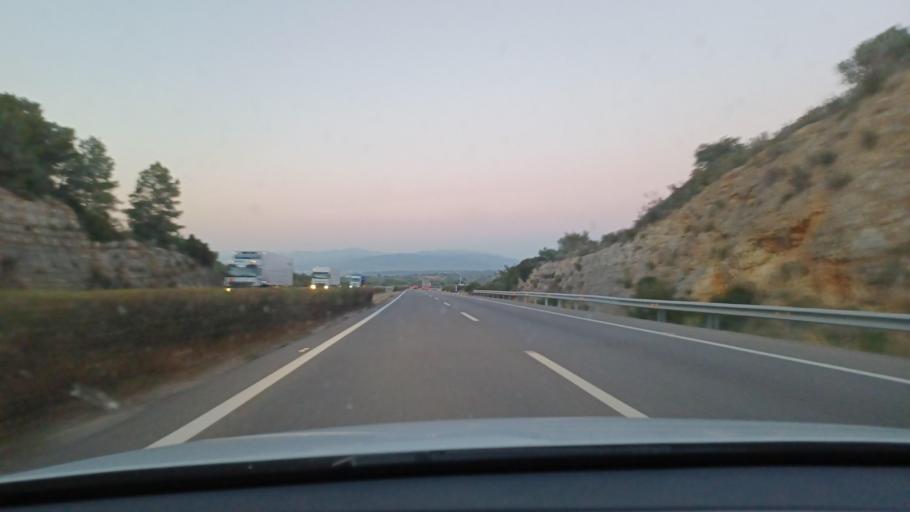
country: ES
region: Catalonia
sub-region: Provincia de Tarragona
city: Masdenverge
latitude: 40.6826
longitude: 0.5251
